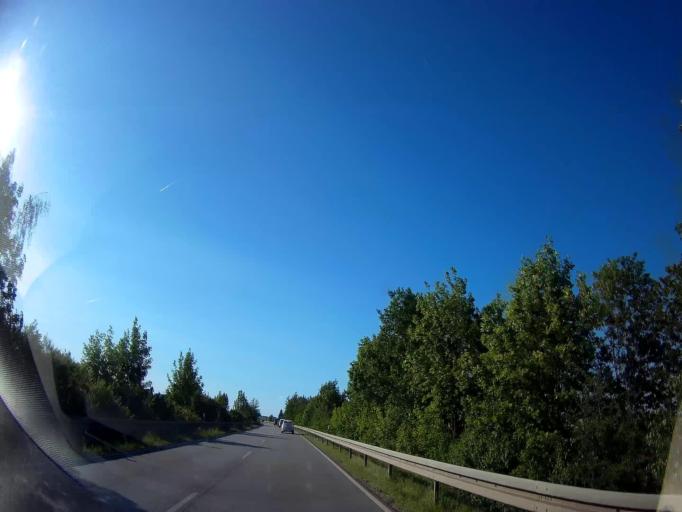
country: DE
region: Bavaria
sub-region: Lower Bavaria
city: Oberschneiding
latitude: 48.7658
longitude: 12.6609
